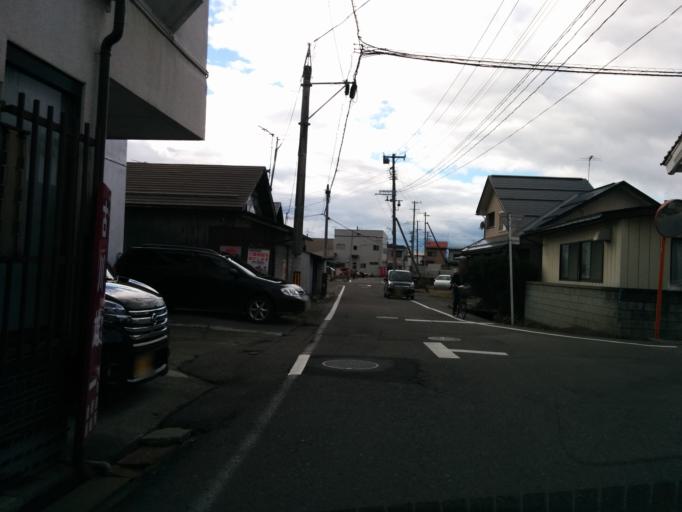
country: JP
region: Fukushima
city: Kitakata
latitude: 37.4907
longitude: 139.9120
